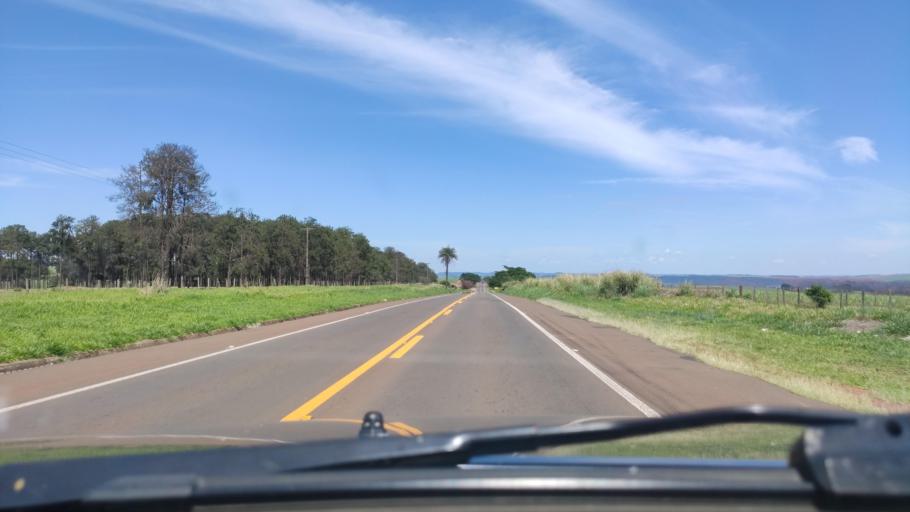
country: BR
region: Sao Paulo
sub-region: Sao Carlos
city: Sao Carlos
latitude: -22.0599
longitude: -47.9738
